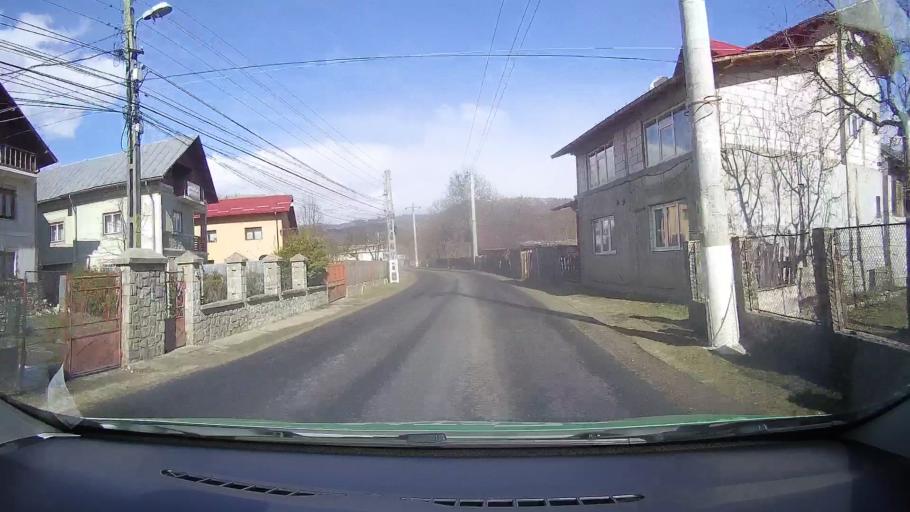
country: RO
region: Dambovita
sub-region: Comuna Runcu
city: Badeni
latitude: 45.1682
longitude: 25.3948
